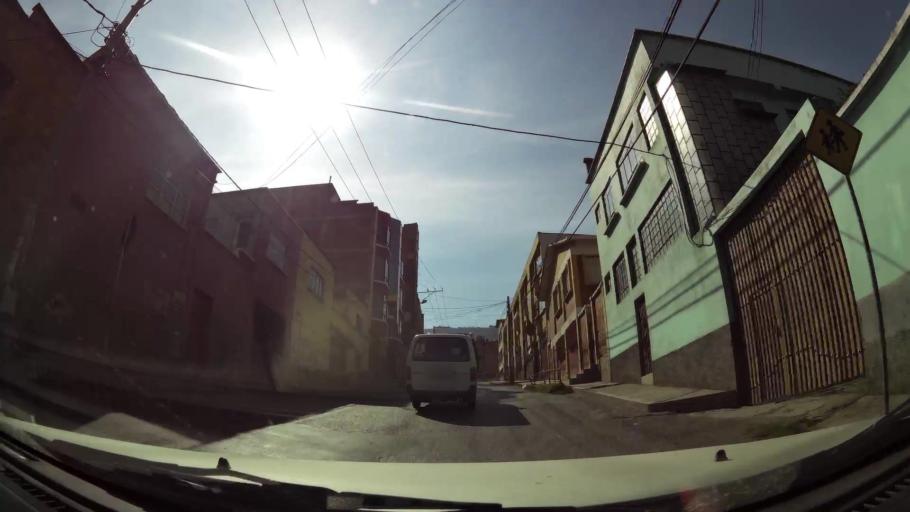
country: BO
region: La Paz
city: La Paz
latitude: -16.4980
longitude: -68.1164
